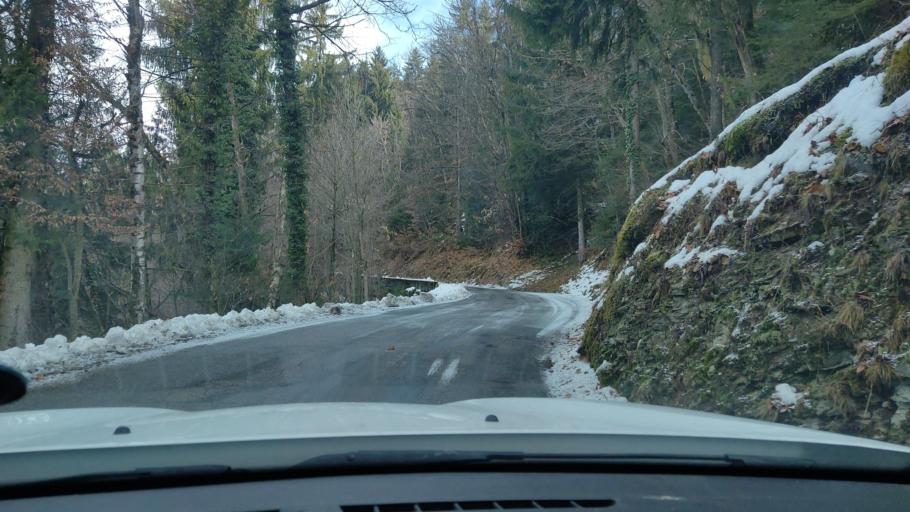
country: FR
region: Rhone-Alpes
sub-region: Departement de la Savoie
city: Marthod
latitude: 45.7009
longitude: 6.4147
